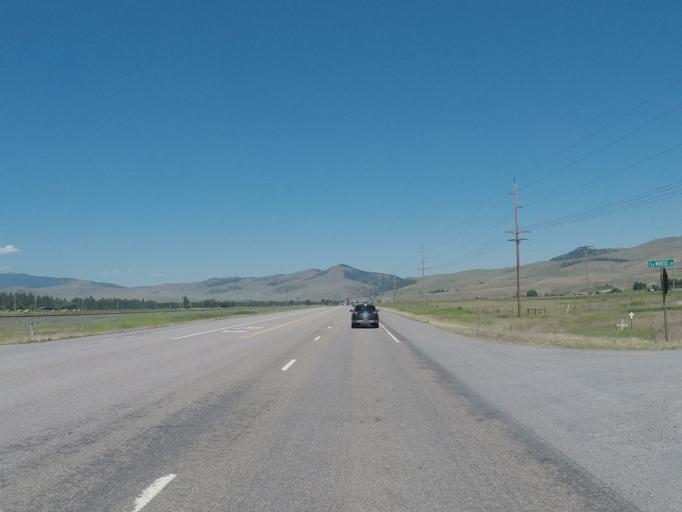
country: US
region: Montana
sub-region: Missoula County
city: Frenchtown
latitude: 47.2070
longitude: -114.1178
